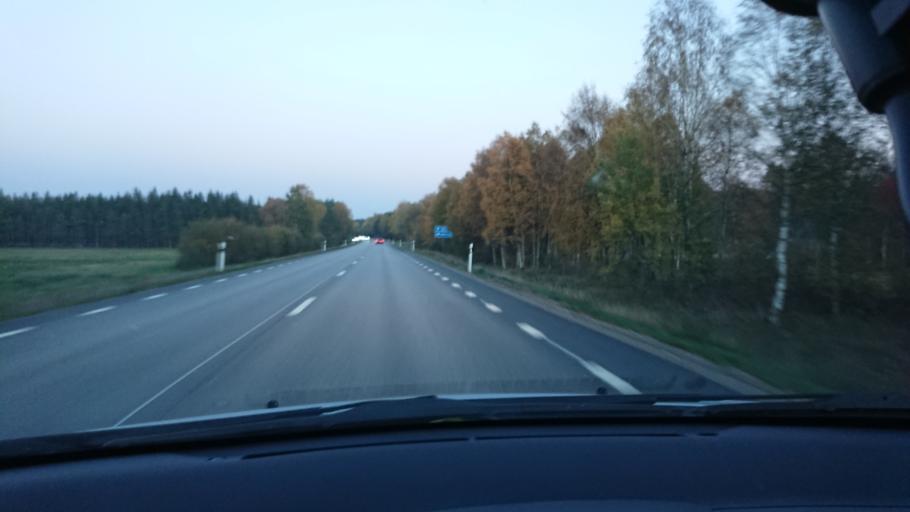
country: SE
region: Kronoberg
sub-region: Markaryds Kommun
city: Stromsnasbruk
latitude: 56.7558
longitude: 13.7435
